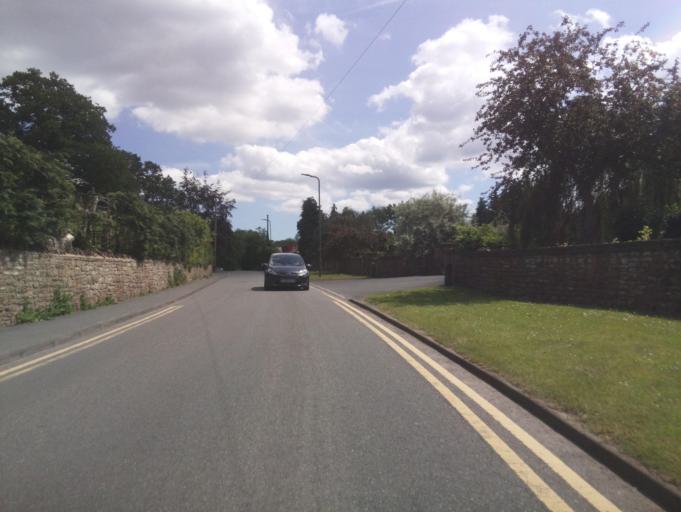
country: GB
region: England
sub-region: Herefordshire
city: Ross on Wye
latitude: 51.9206
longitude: -2.5884
